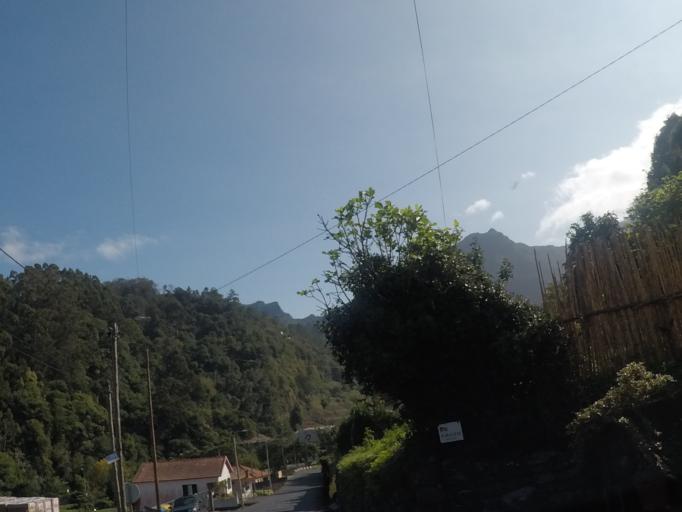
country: PT
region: Madeira
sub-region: Sao Vicente
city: Sao Vicente
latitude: 32.7846
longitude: -17.0347
